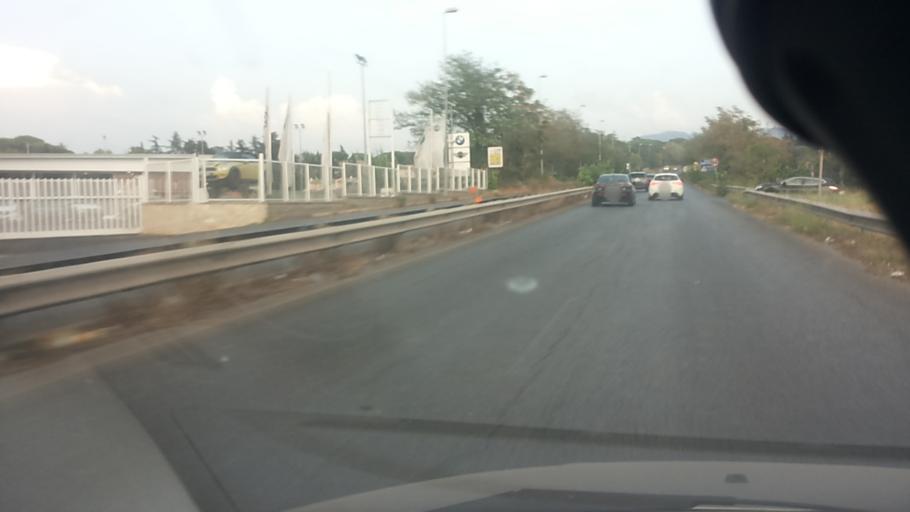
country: IT
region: Latium
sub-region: Citta metropolitana di Roma Capitale
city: Frascati
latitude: 41.8229
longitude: 12.6378
